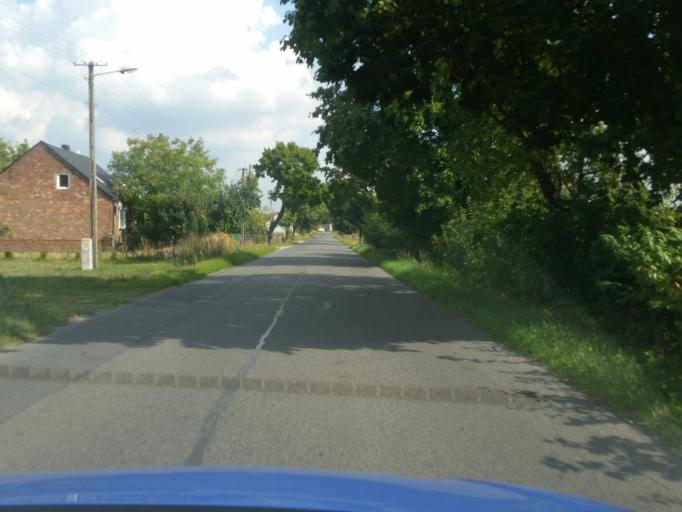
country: PL
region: Silesian Voivodeship
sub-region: Powiat czestochowski
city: Klomnice
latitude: 50.9647
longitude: 19.3313
